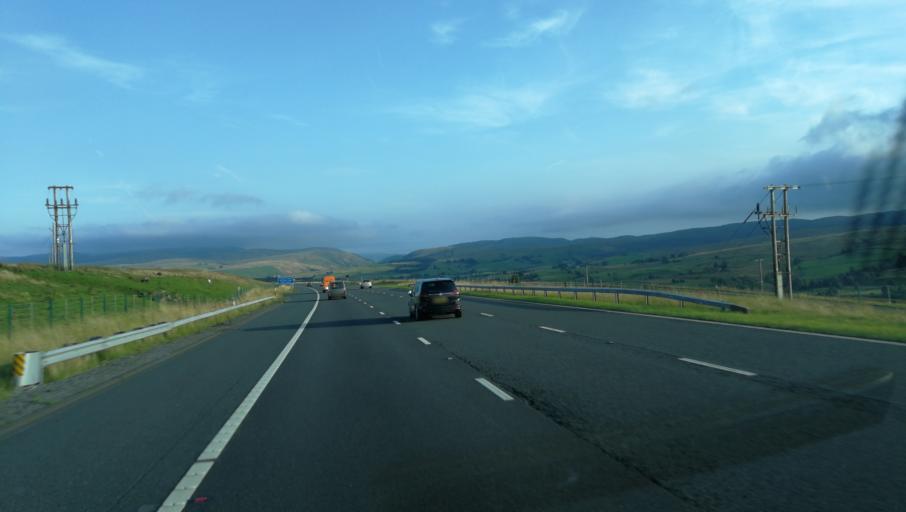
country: GB
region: England
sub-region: Cumbria
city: Appleby-in-Westmorland
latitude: 54.4732
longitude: -2.6299
